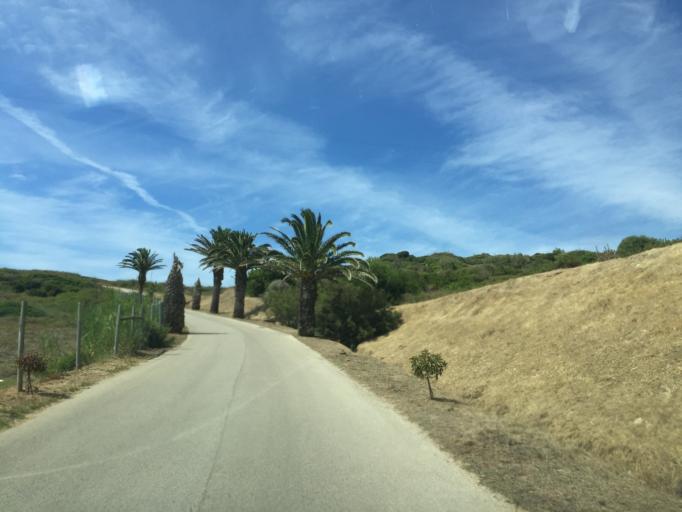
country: PT
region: Lisbon
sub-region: Torres Vedras
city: A dos Cunhados
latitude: 39.1804
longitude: -9.3519
